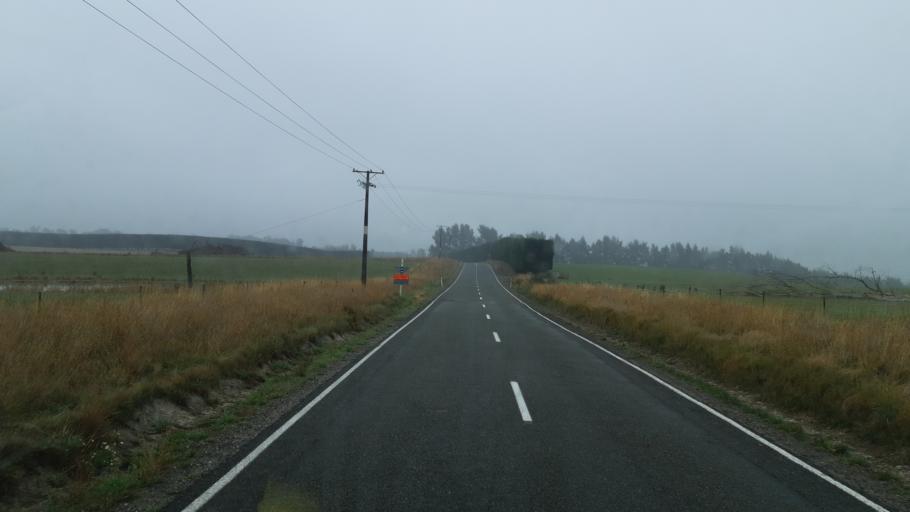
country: NZ
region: Otago
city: Oamaru
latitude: -44.9277
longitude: 170.8061
